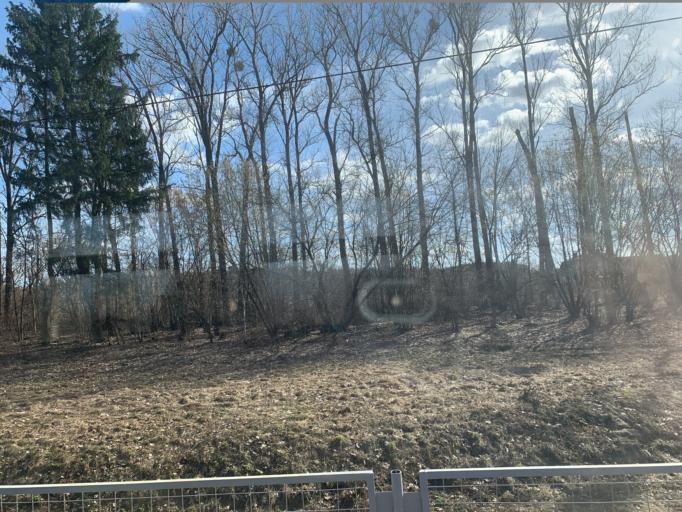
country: BY
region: Minsk
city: Stowbtsy
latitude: 53.5139
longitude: 26.8691
